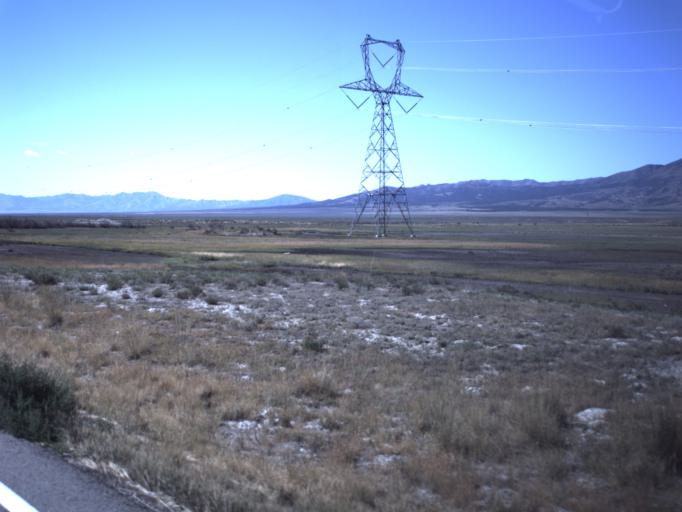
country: US
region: Utah
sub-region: Tooele County
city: Tooele
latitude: 40.3265
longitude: -112.4076
